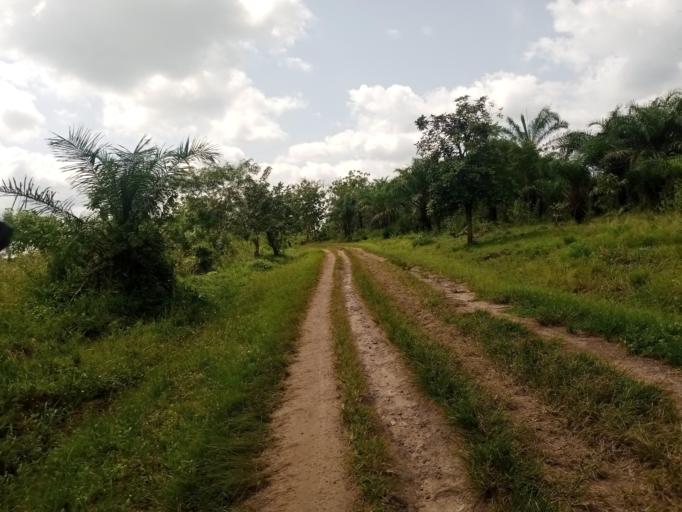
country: TG
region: Maritime
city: Tsevie
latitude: 6.5211
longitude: 1.0522
